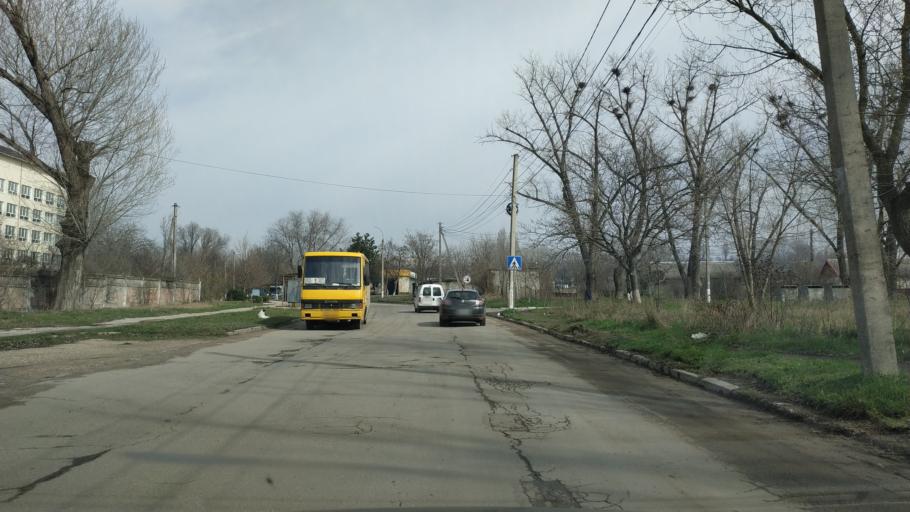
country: MD
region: Cahul
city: Cahul
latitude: 45.8911
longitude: 28.1991
